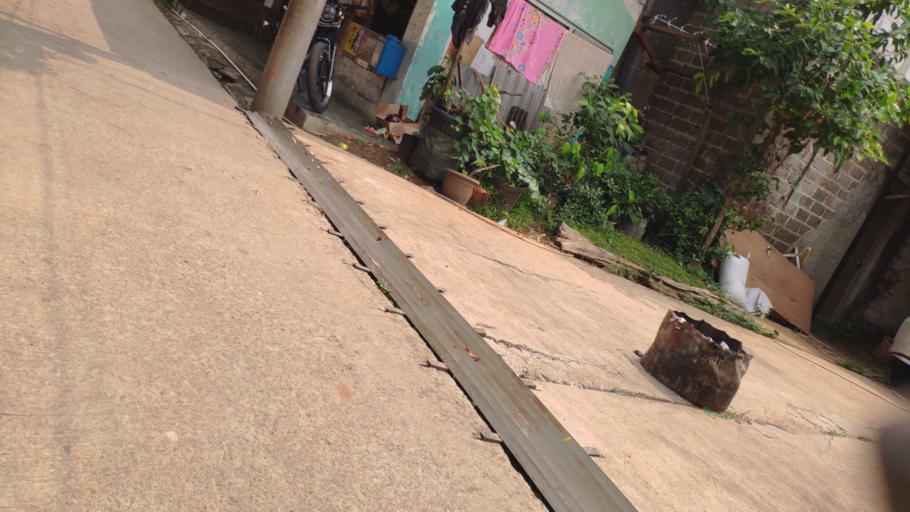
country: ID
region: West Java
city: Depok
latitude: -6.3700
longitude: 106.8012
